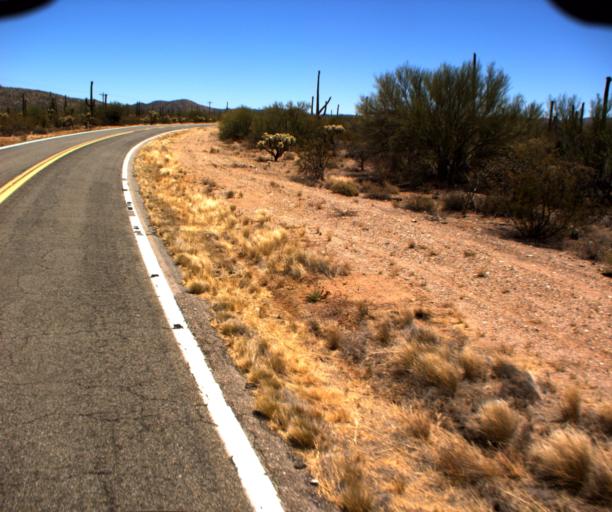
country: US
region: Arizona
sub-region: Pima County
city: Sells
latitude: 32.1768
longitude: -112.2572
